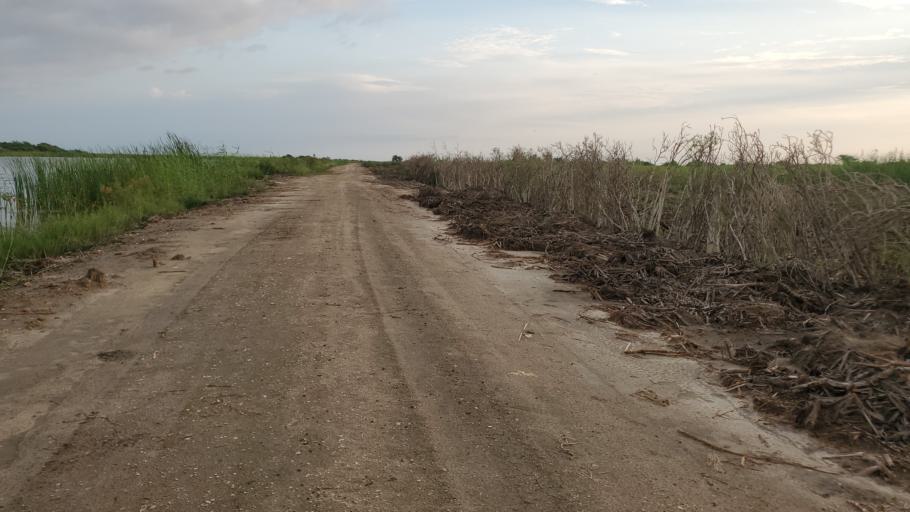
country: SN
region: Saint-Louis
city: Saint-Louis
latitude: 16.0119
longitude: -16.4008
